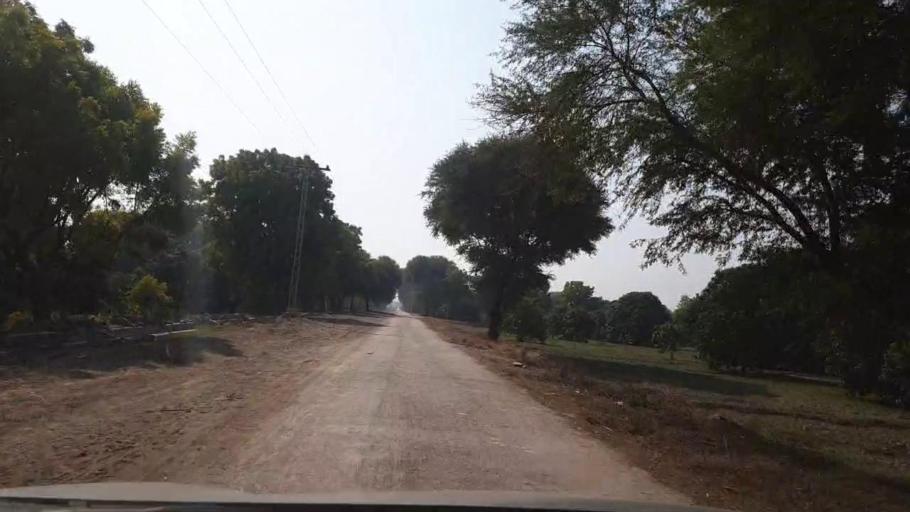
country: PK
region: Sindh
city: Tando Allahyar
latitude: 25.5105
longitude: 68.7861
